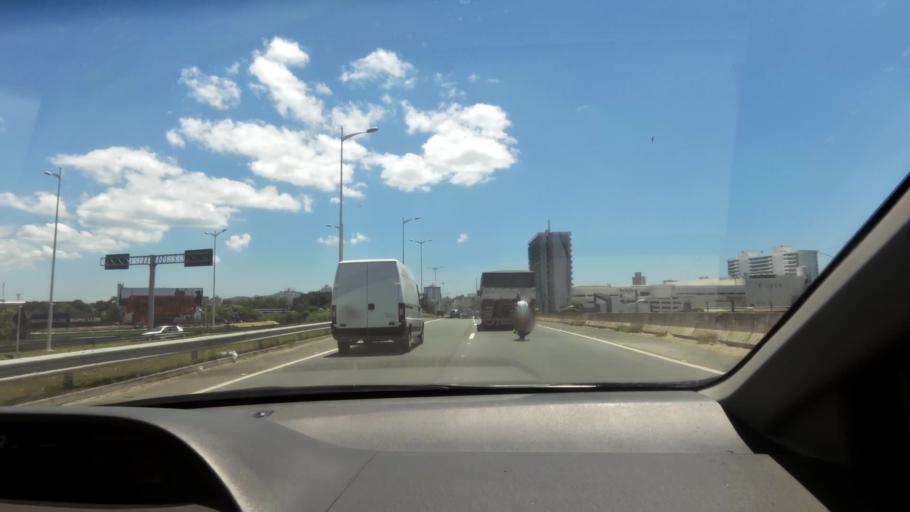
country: BR
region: Bahia
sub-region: Prado
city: Prado
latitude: -17.2895
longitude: -39.0292
